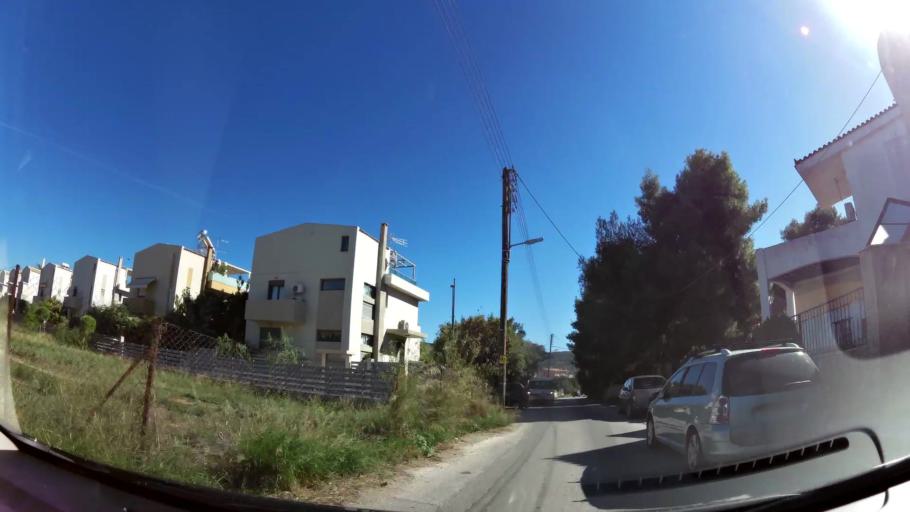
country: GR
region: Attica
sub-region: Nomarchia Anatolikis Attikis
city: Vari
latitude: 37.8388
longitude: 23.8147
